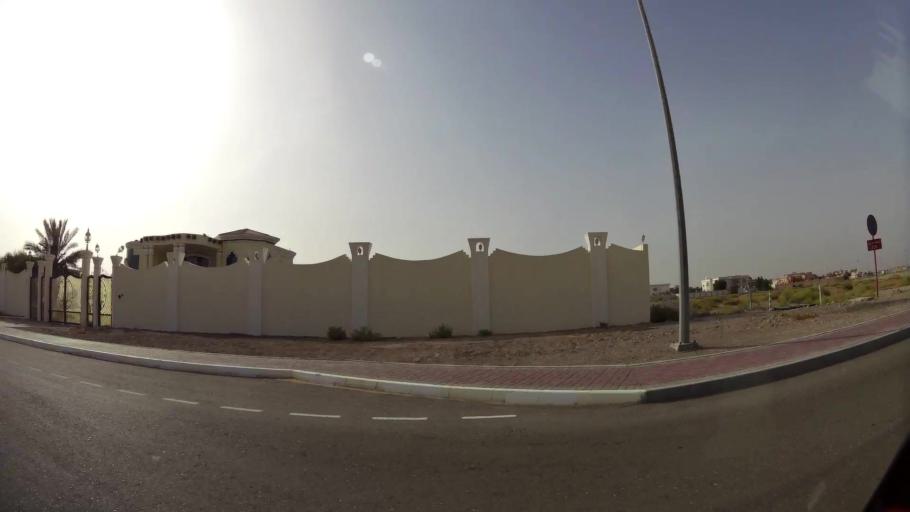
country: AE
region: Abu Dhabi
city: Al Ain
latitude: 24.2020
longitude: 55.6310
